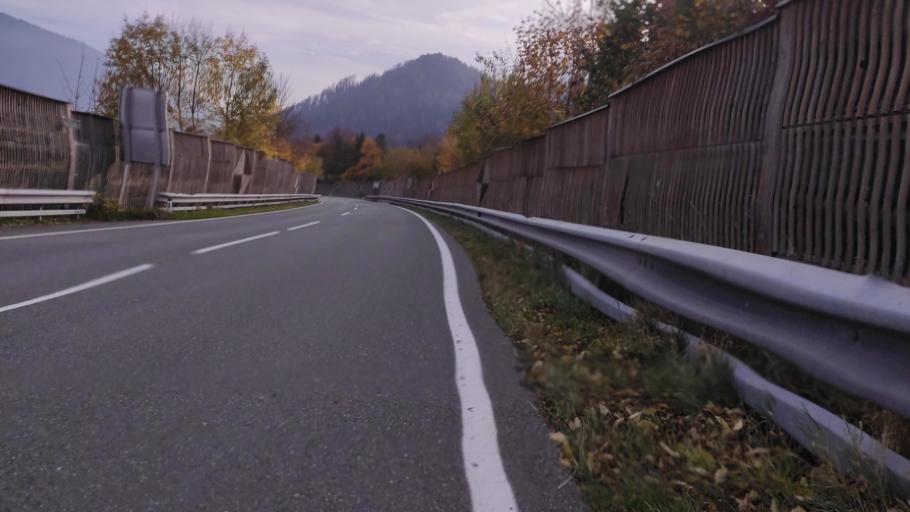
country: AT
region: Salzburg
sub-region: Politischer Bezirk Salzburg-Umgebung
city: Ebenau
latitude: 47.7927
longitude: 13.1735
